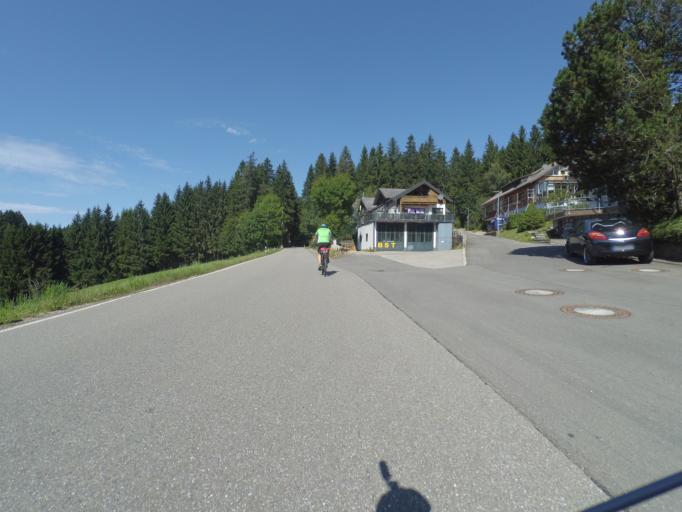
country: DE
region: Baden-Wuerttemberg
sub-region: Freiburg Region
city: Gutenbach
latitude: 48.0303
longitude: 8.1770
